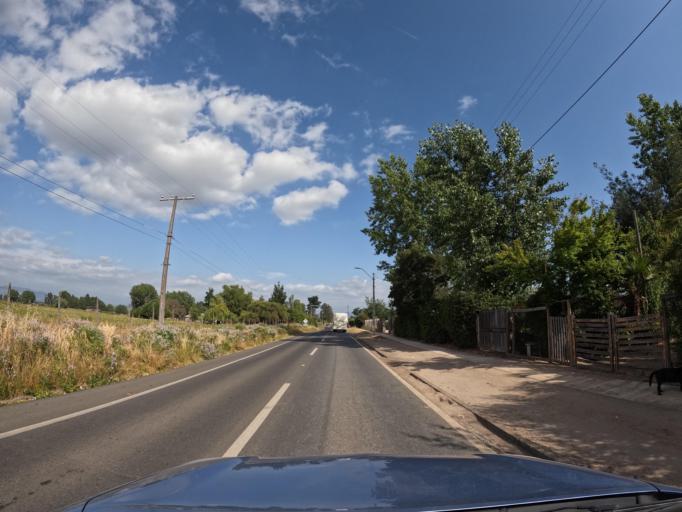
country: CL
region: Maule
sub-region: Provincia de Curico
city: Molina
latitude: -35.2652
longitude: -71.3189
